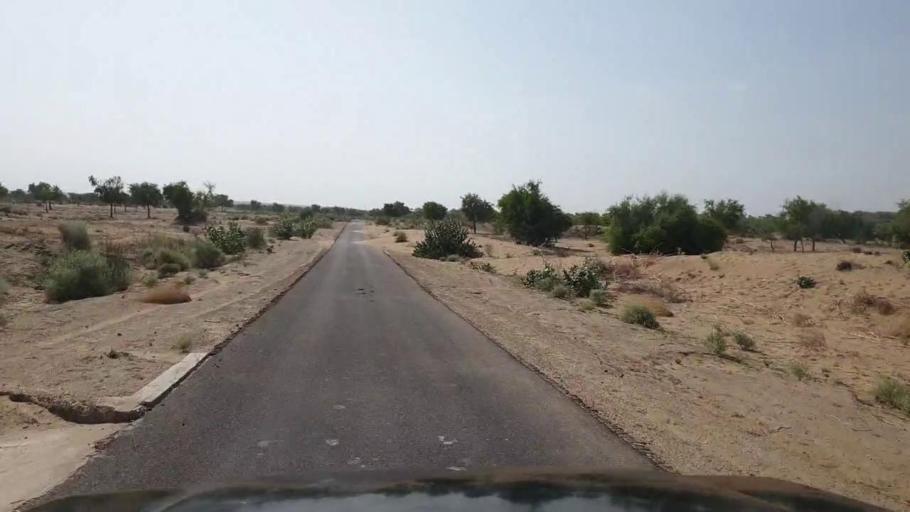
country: PK
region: Sindh
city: Islamkot
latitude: 24.9397
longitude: 70.0799
